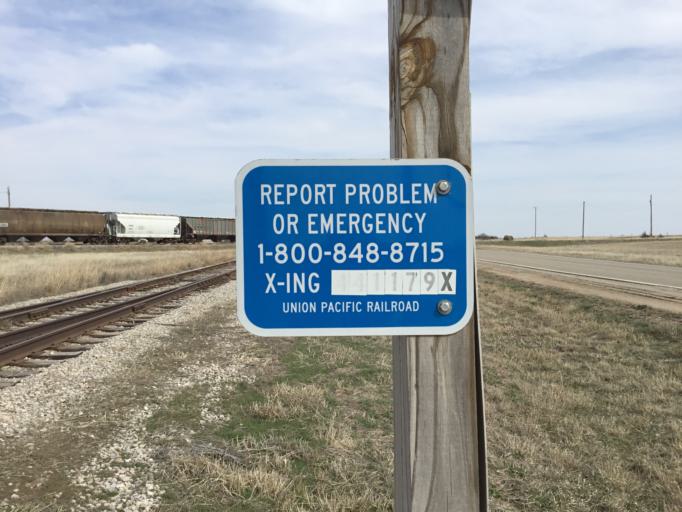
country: US
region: Kansas
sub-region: Ellsworth County
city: Ellsworth
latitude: 38.7252
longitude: -98.1270
